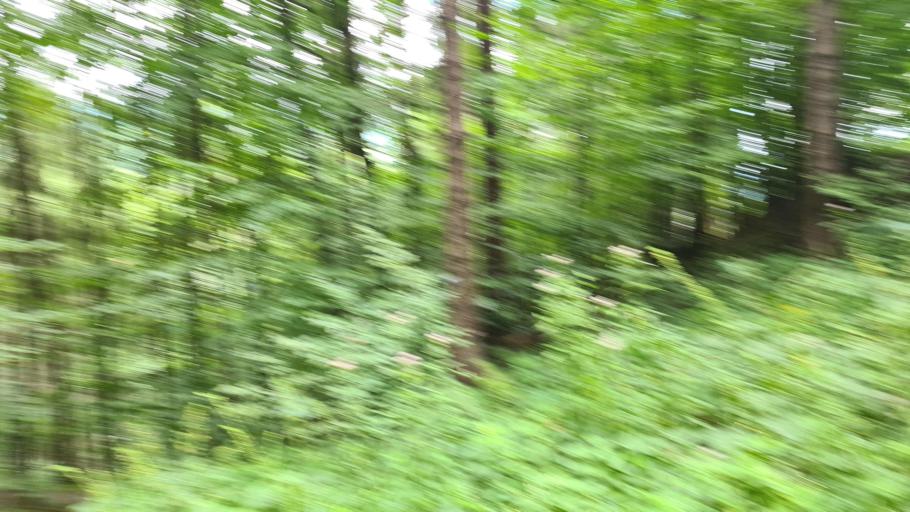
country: PL
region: Lesser Poland Voivodeship
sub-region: Powiat nowosadecki
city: Piwniczna-Zdroj
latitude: 49.4362
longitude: 20.7206
